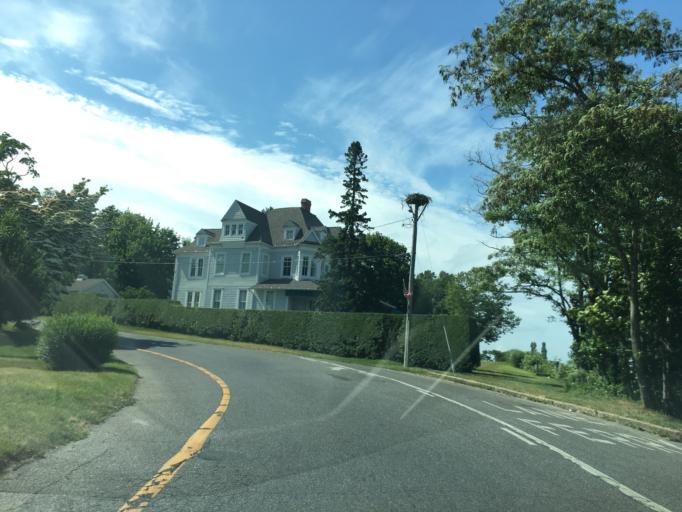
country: US
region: New York
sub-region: Suffolk County
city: Shelter Island Heights
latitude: 41.0844
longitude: -72.3534
